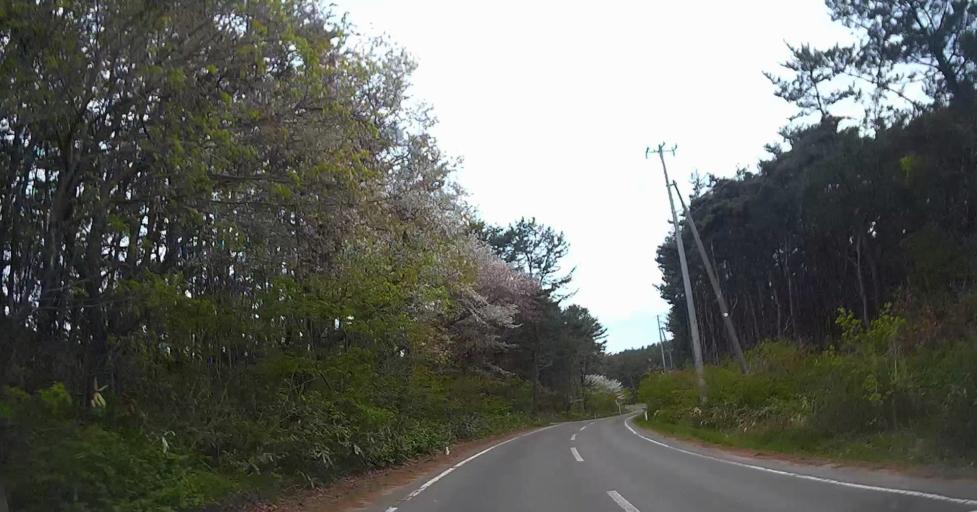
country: JP
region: Aomori
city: Shimokizukuri
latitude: 40.9369
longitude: 140.3357
